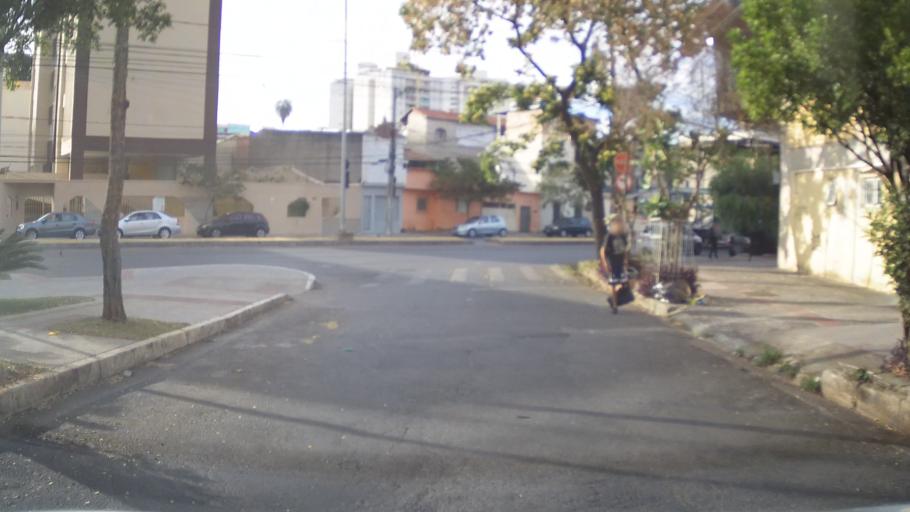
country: BR
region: Minas Gerais
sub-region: Belo Horizonte
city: Belo Horizonte
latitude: -19.8554
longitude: -43.9590
